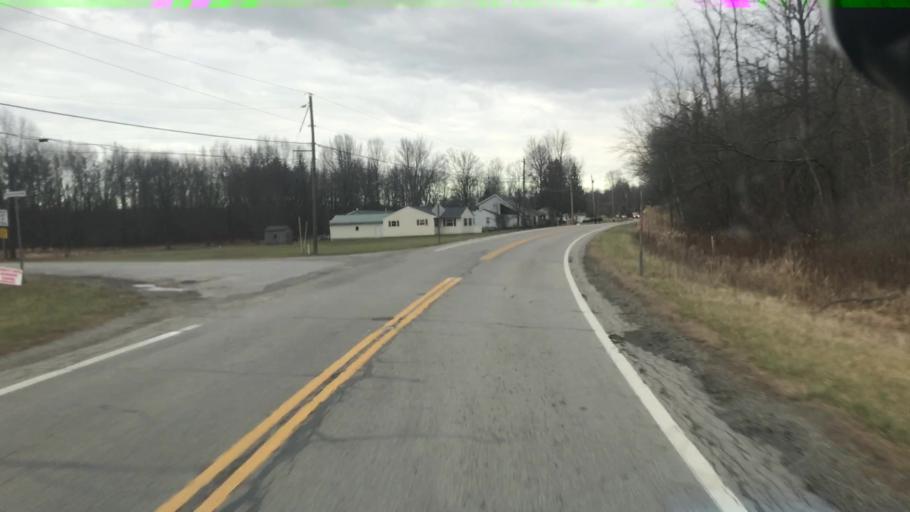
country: US
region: Ohio
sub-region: Portage County
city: Windham
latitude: 41.2700
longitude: -80.9774
